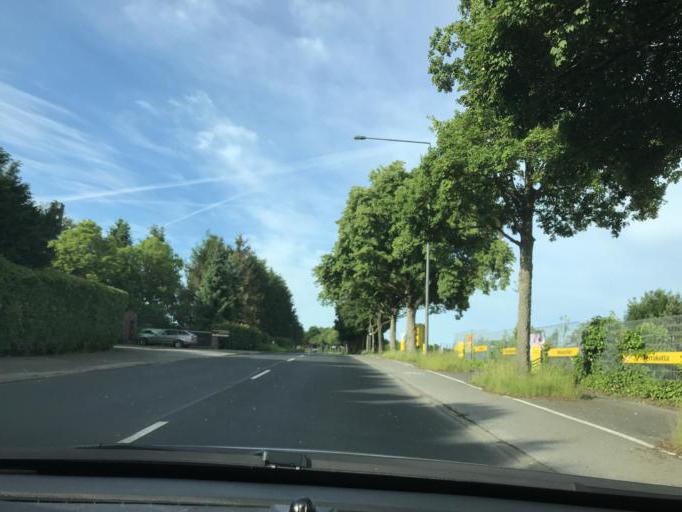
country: DE
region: North Rhine-Westphalia
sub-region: Regierungsbezirk Koln
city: Aachen
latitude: 50.7463
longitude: 6.1259
